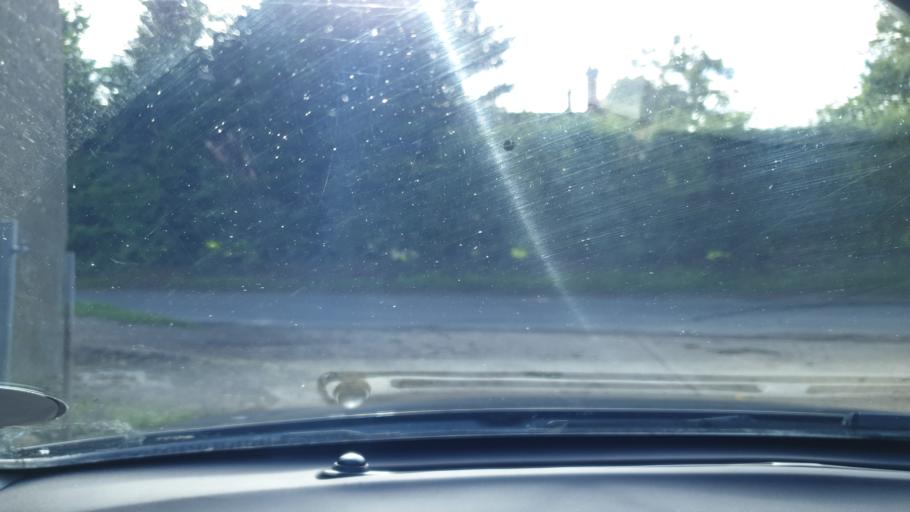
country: GB
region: England
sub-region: Essex
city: Manningtree
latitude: 51.9011
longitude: 1.0368
